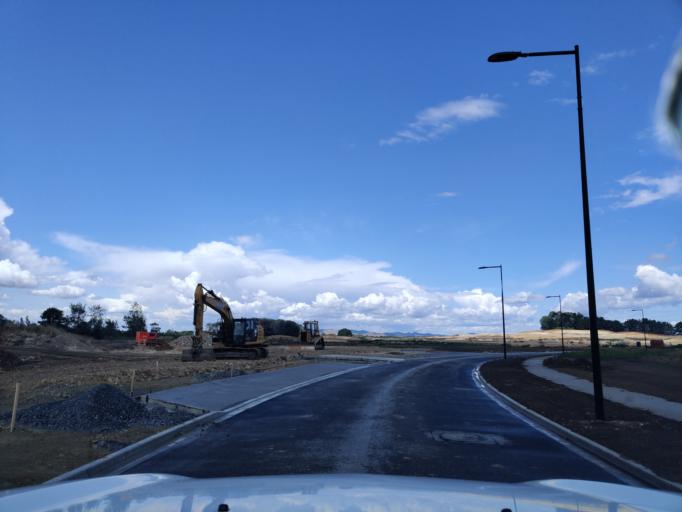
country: NZ
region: Waikato
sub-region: Waikato District
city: Te Kauwhata
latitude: -37.4103
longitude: 175.1531
